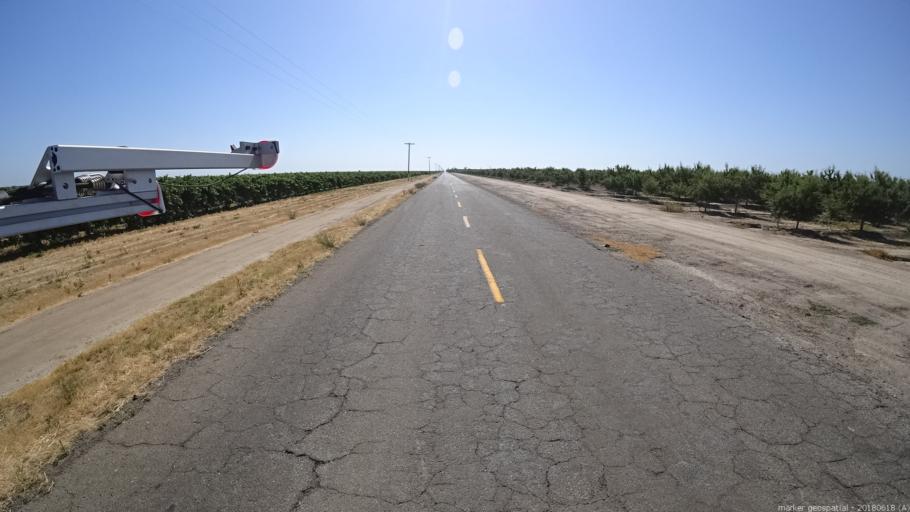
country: US
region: California
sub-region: Madera County
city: Parkwood
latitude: 36.8366
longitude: -120.1941
